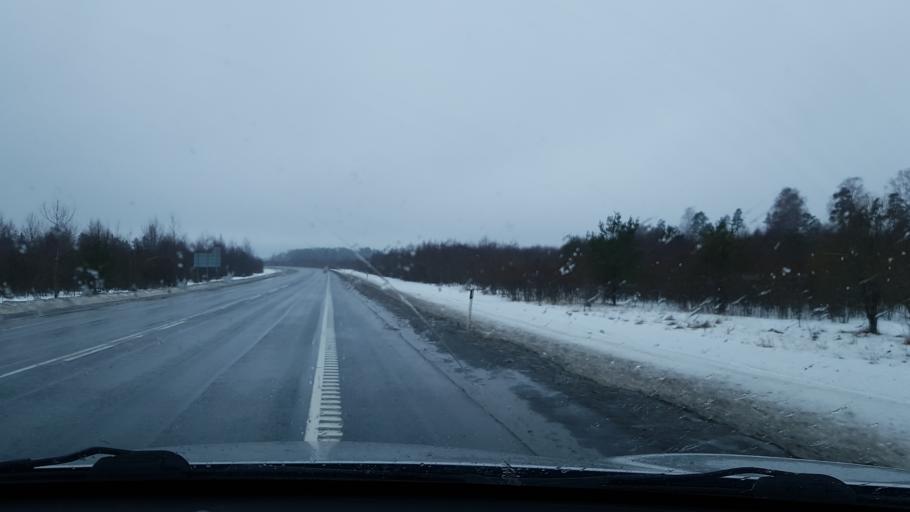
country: EE
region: Raplamaa
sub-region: Kohila vald
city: Kohila
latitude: 59.1784
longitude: 24.7785
